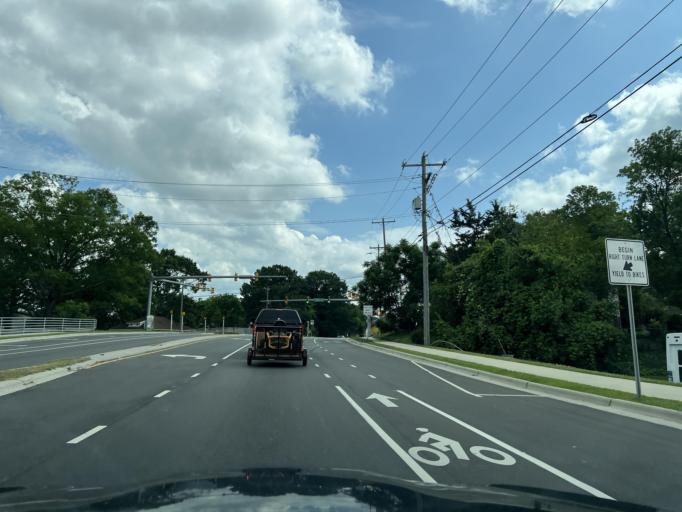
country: US
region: North Carolina
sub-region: Durham County
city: Durham
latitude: 35.9912
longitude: -78.8862
